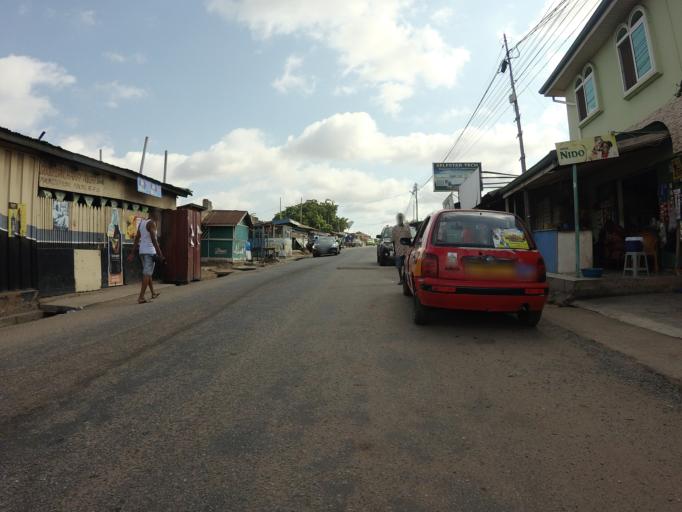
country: GH
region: Greater Accra
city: Dome
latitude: 5.6128
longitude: -0.2333
